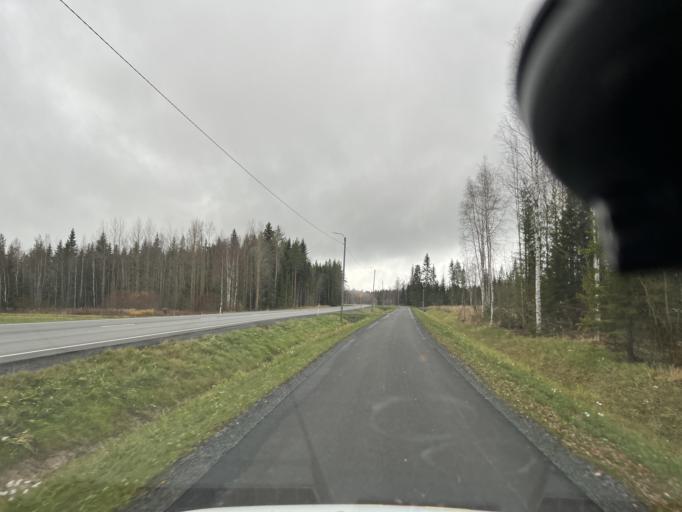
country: FI
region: Northern Ostrobothnia
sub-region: Ylivieska
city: Sievi
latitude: 63.9395
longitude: 24.5315
